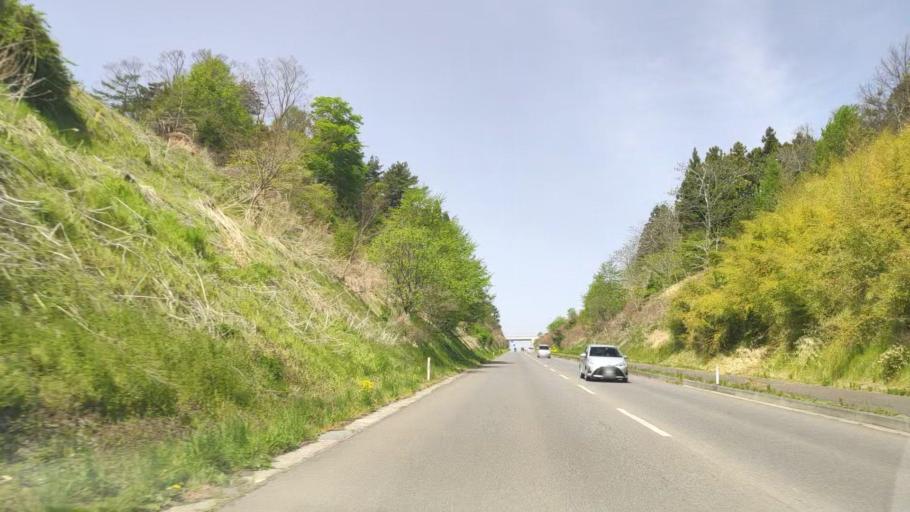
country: JP
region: Aomori
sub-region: Hachinohe Shi
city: Uchimaru
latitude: 40.5234
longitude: 141.4150
